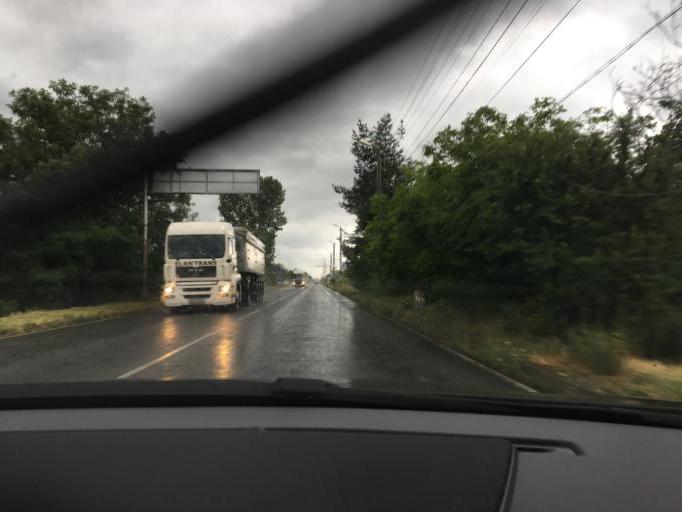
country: BG
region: Kyustendil
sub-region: Obshtina Kyustendil
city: Kyustendil
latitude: 42.2723
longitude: 22.6501
